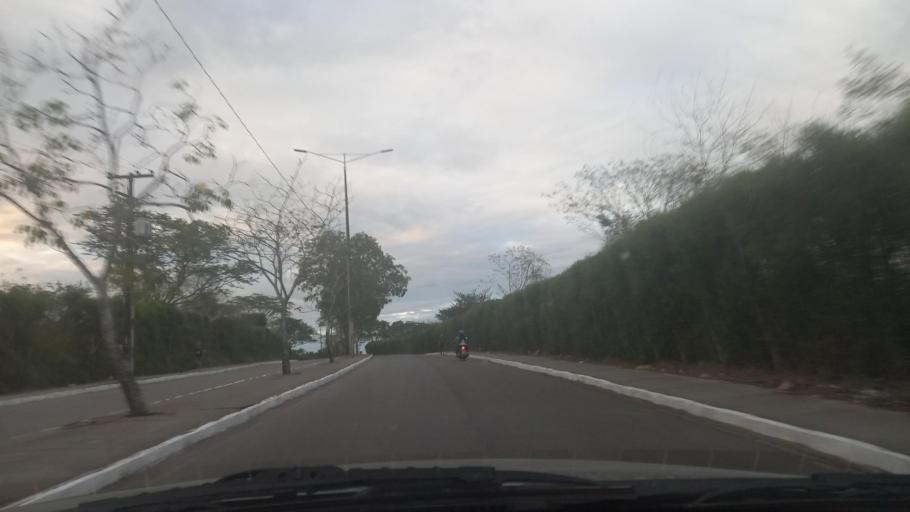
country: BR
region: Pernambuco
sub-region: Caruaru
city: Caruaru
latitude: -8.2577
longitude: -35.9636
